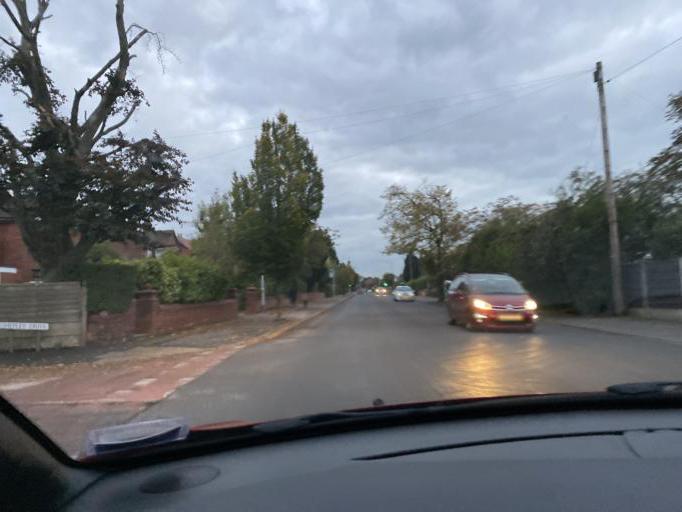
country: GB
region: England
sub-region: Borough of Stockport
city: Hazel Grove
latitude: 53.3736
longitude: -2.1231
